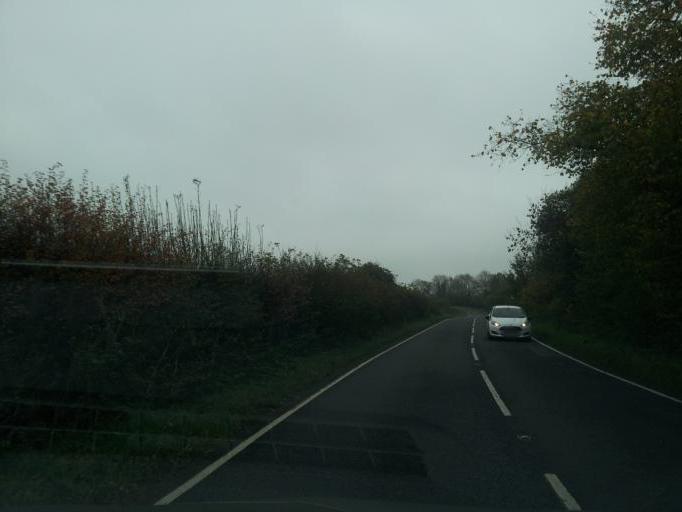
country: GB
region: England
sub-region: Buckinghamshire
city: Buckingham
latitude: 52.0038
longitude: -1.0049
